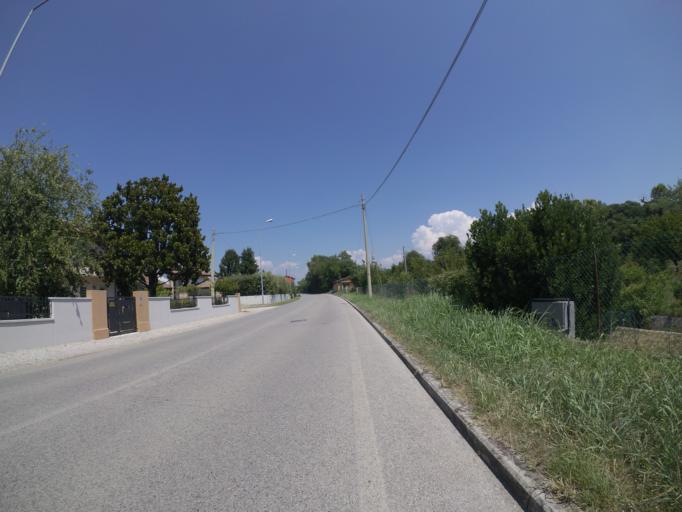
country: IT
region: Friuli Venezia Giulia
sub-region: Provincia di Udine
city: Mortegliano
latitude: 45.9380
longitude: 13.1646
